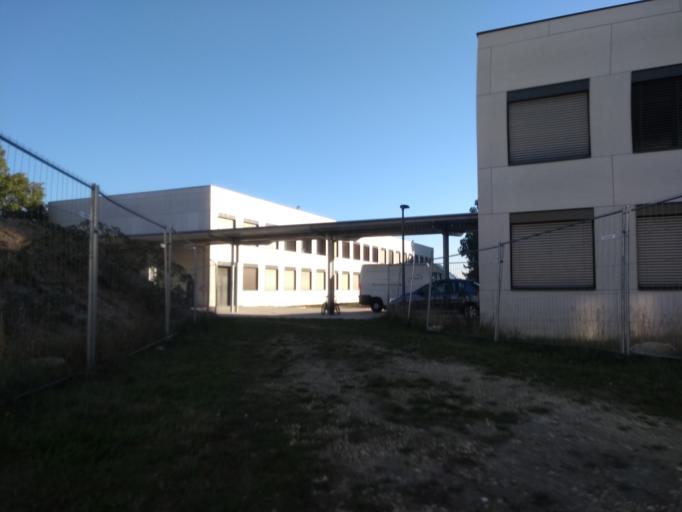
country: FR
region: Aquitaine
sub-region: Departement de la Gironde
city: Talence
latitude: 44.8030
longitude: -0.6098
